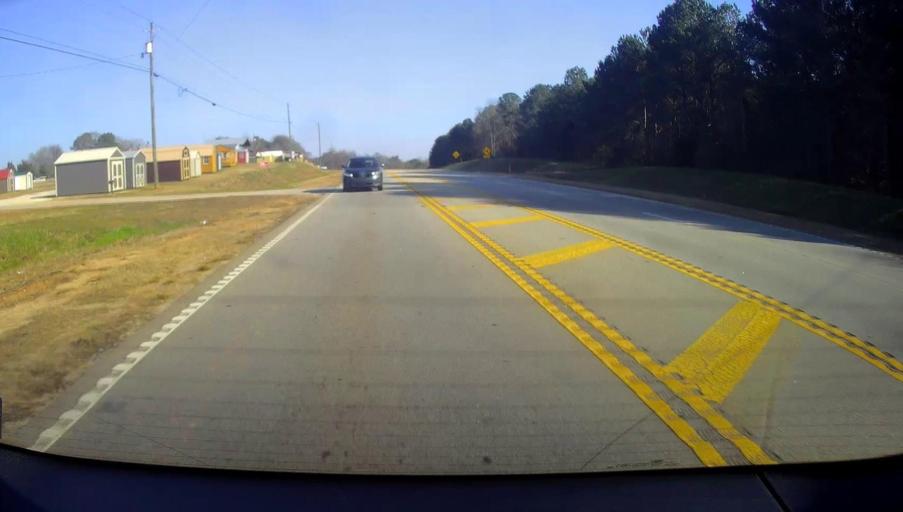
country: US
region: Georgia
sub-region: Butts County
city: Jackson
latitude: 33.3261
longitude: -84.0041
